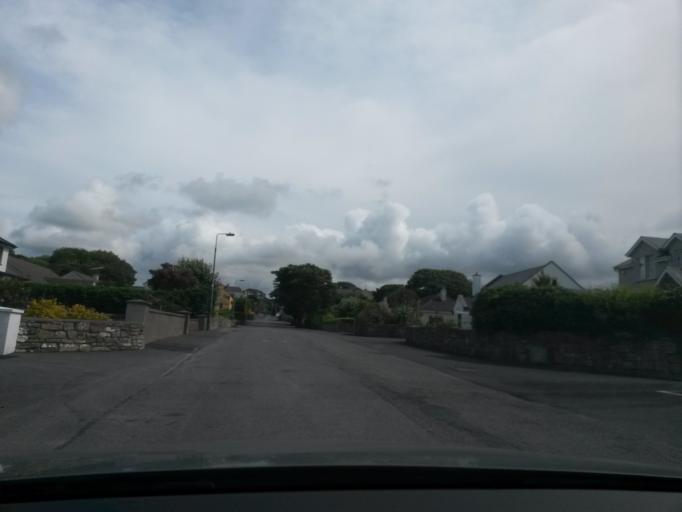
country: IE
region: Connaught
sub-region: Sligo
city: Sligo
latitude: 54.4314
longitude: -8.4555
